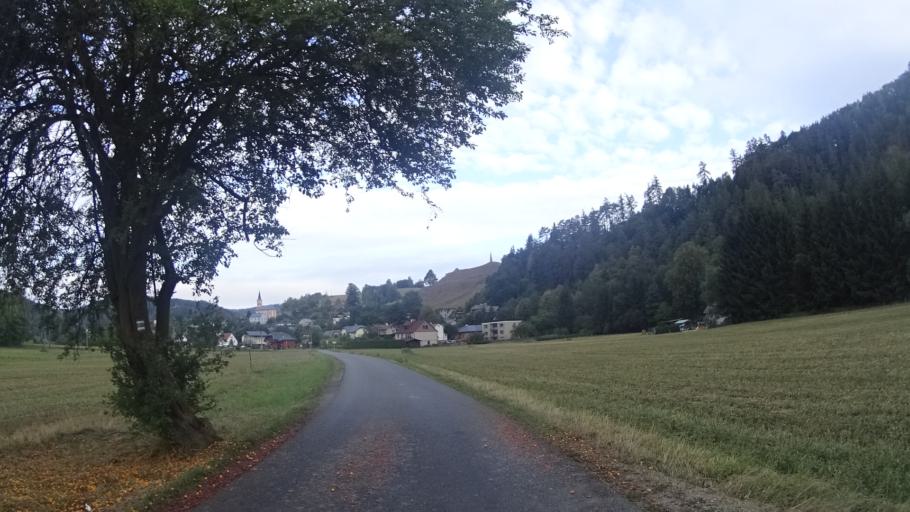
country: CZ
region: Olomoucky
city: Stity
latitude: 49.8746
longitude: 16.7829
